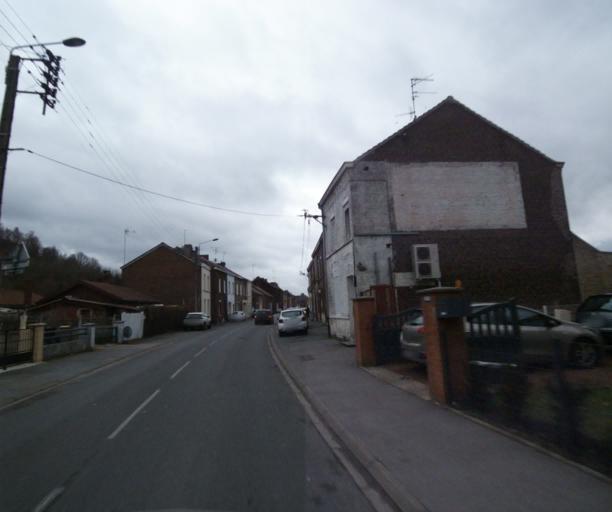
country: FR
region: Nord-Pas-de-Calais
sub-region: Departement du Nord
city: Anzin
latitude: 50.3830
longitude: 3.5139
